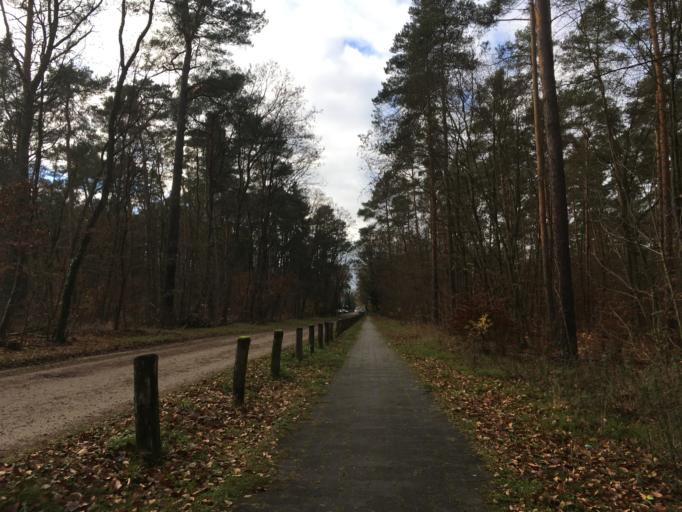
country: DE
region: Brandenburg
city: Waldsieversdorf
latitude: 52.5470
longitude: 14.0774
